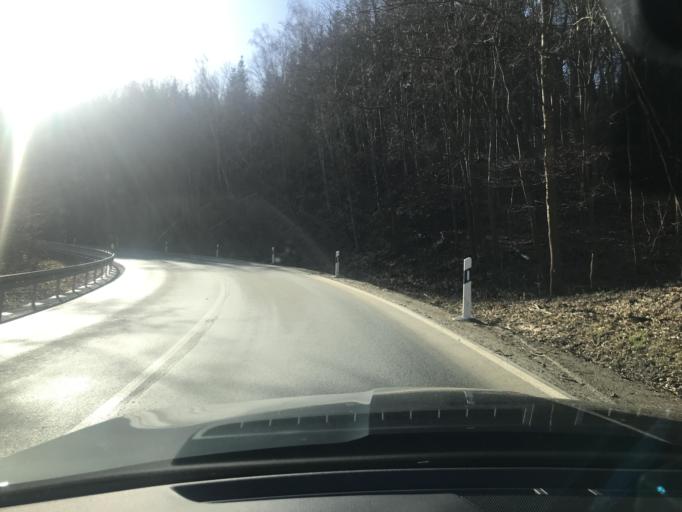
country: DE
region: Saxony-Anhalt
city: Blankenburg
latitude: 51.7892
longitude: 10.9401
